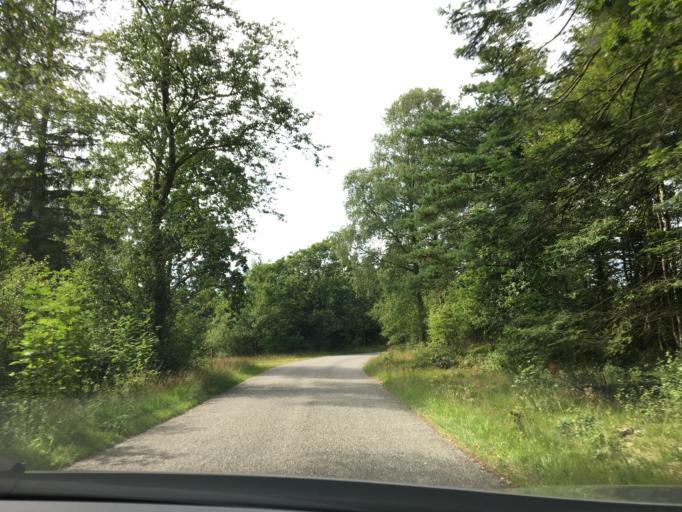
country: DK
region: South Denmark
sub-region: Varde Kommune
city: Oksbol
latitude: 55.7442
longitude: 8.2499
